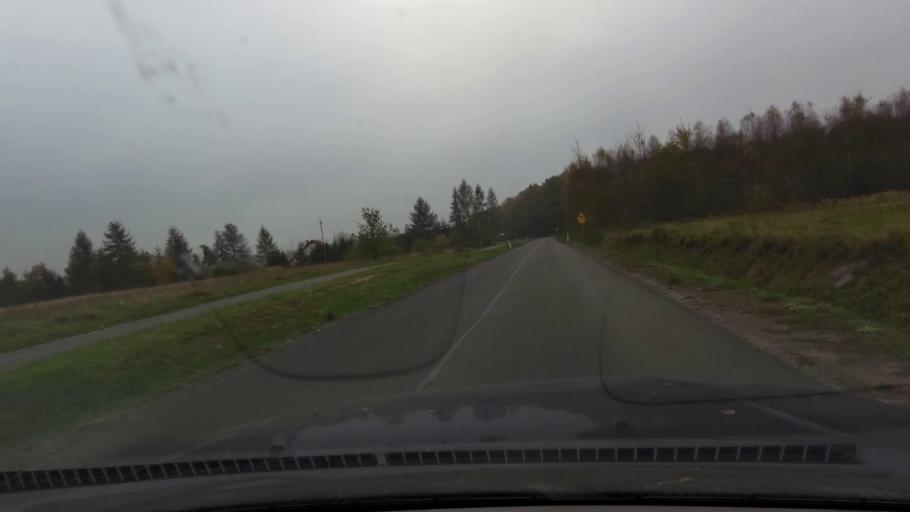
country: PL
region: West Pomeranian Voivodeship
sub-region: Powiat goleniowski
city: Goleniow
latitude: 53.5793
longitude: 14.8000
